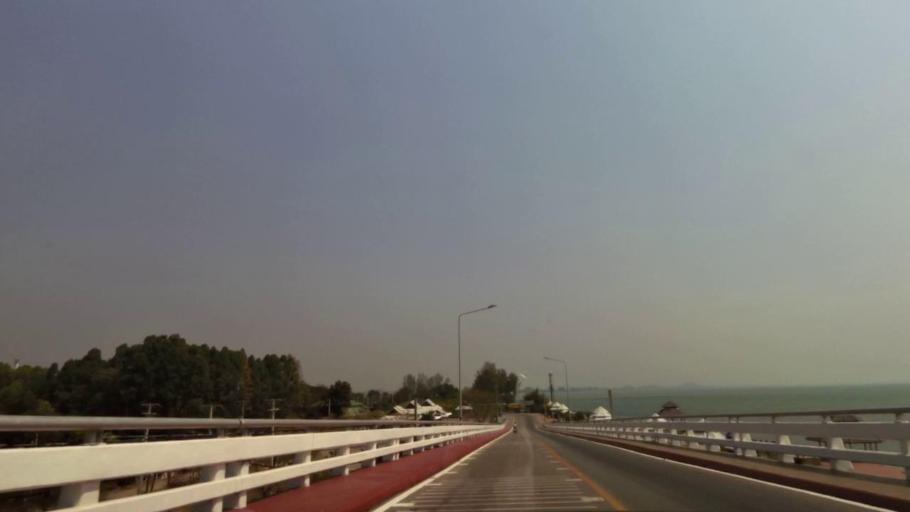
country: TH
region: Chanthaburi
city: Tha Mai
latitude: 12.5392
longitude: 101.9501
